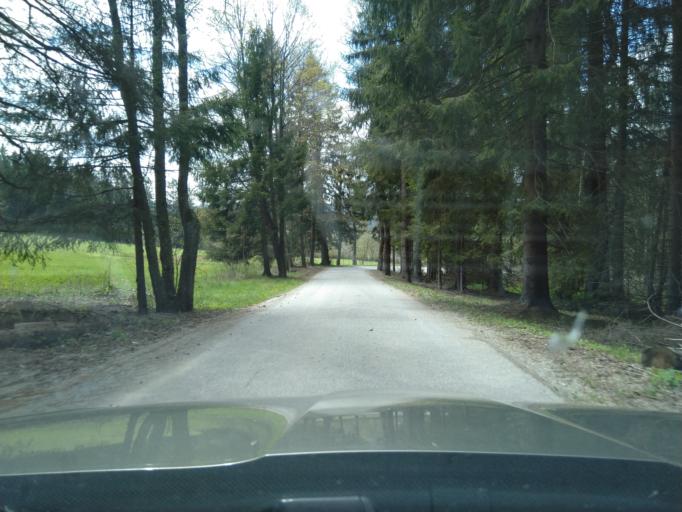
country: CZ
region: Jihocesky
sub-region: Okres Prachatice
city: Borova Lada
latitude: 48.9973
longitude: 13.6843
